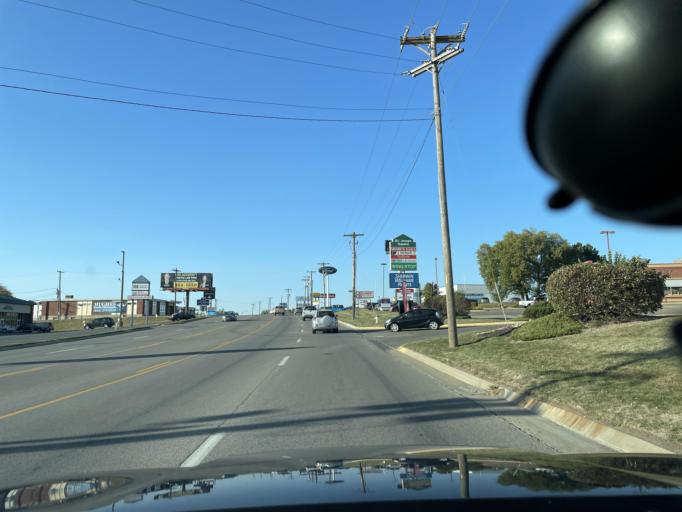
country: US
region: Missouri
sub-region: Buchanan County
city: Saint Joseph
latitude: 39.7832
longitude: -94.8030
